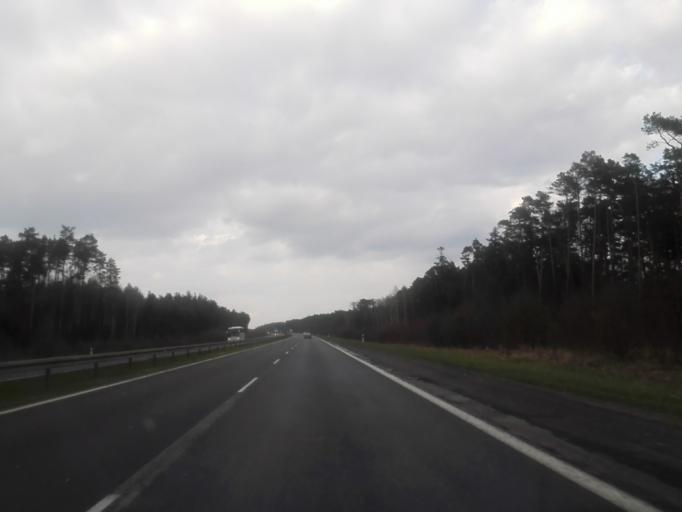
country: PL
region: Lodz Voivodeship
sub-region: Powiat radomszczanski
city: Gomunice
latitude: 51.1580
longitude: 19.4487
